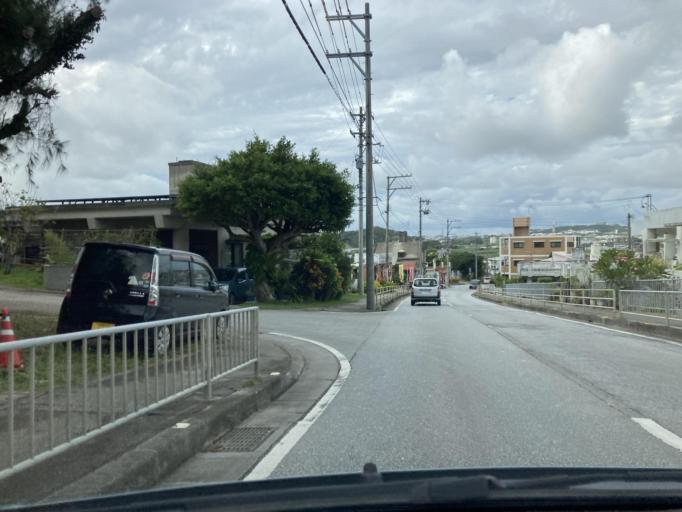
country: JP
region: Okinawa
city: Tomigusuku
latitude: 26.1792
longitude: 127.7434
